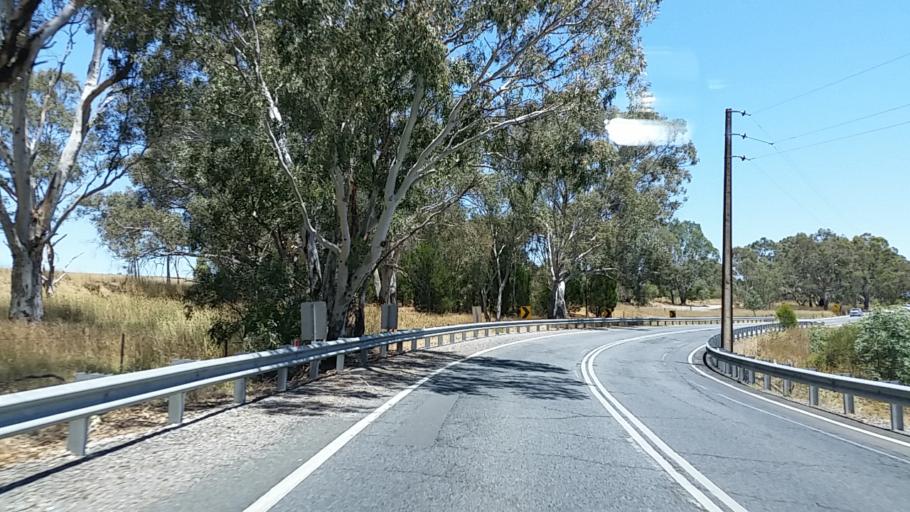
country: AU
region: South Australia
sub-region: Adelaide Hills
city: Birdwood
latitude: -34.8021
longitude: 138.9979
